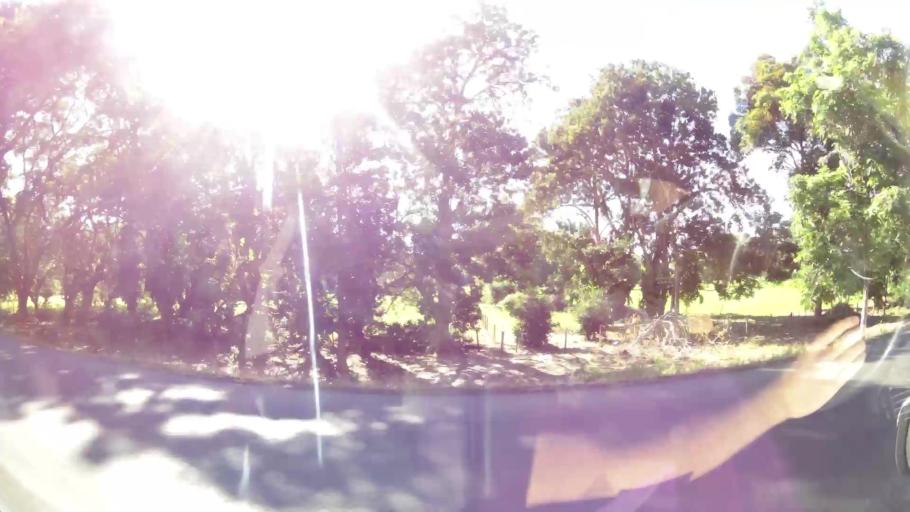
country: CR
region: Puntarenas
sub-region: Canton de Garabito
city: Jaco
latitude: 9.6077
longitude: -84.6157
